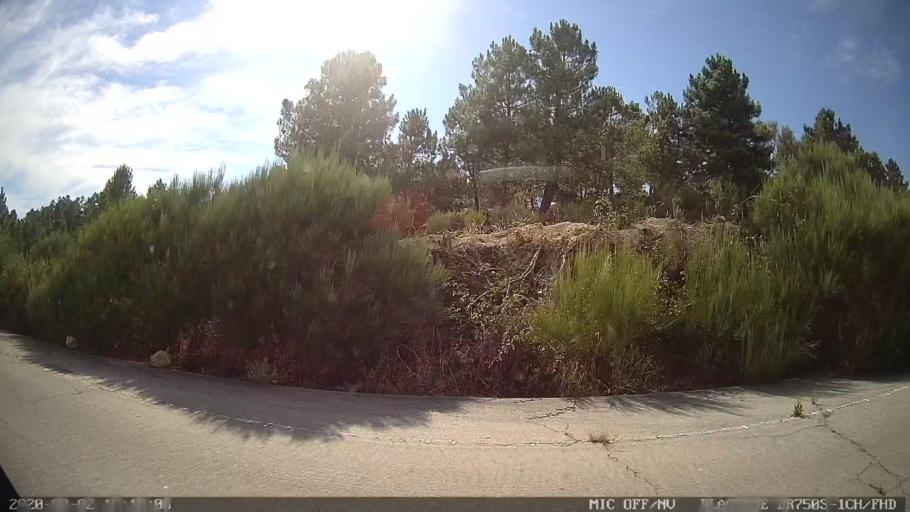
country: PT
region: Vila Real
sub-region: Murca
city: Murca
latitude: 41.3689
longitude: -7.5523
